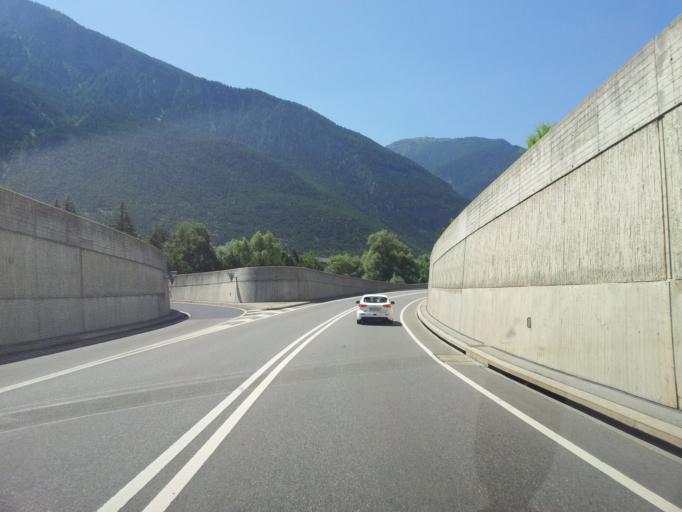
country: CH
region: Valais
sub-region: Brig District
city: Brig
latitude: 46.3160
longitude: 7.9780
